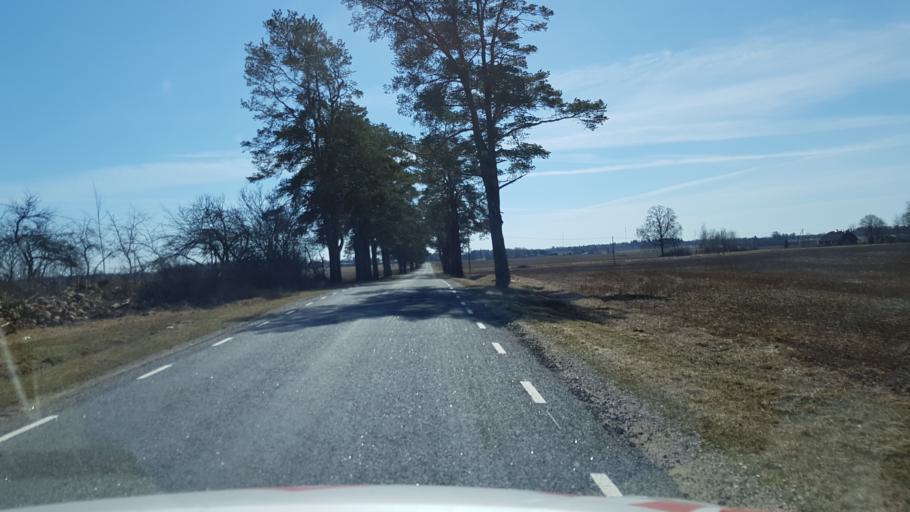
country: EE
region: Laeaene-Virumaa
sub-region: Vinni vald
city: Vinni
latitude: 59.1131
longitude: 26.5240
